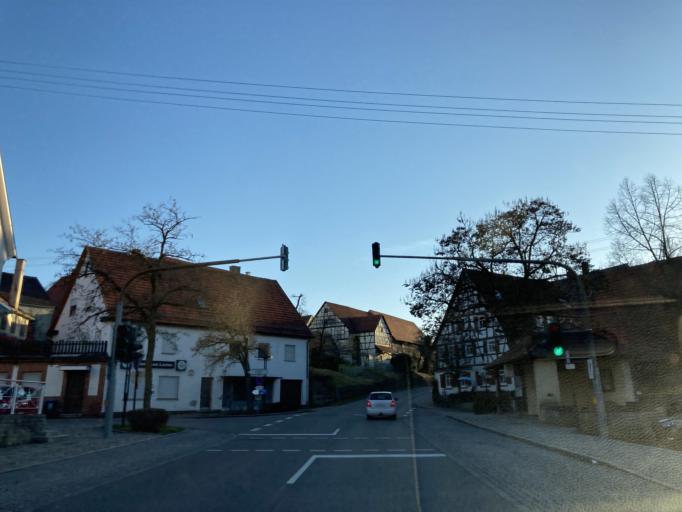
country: DE
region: Baden-Wuerttemberg
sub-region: Tuebingen Region
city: Gomaringen
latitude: 48.4159
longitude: 9.1085
